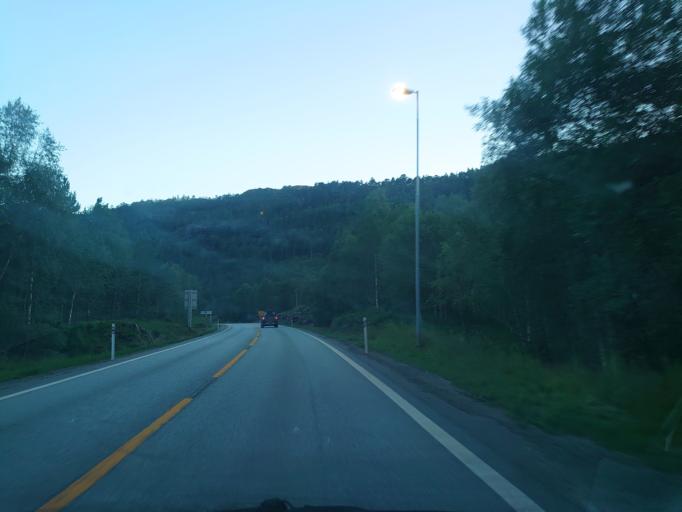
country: NO
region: Hordaland
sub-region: Osteroy
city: Lonevag
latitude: 60.6639
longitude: 5.4847
